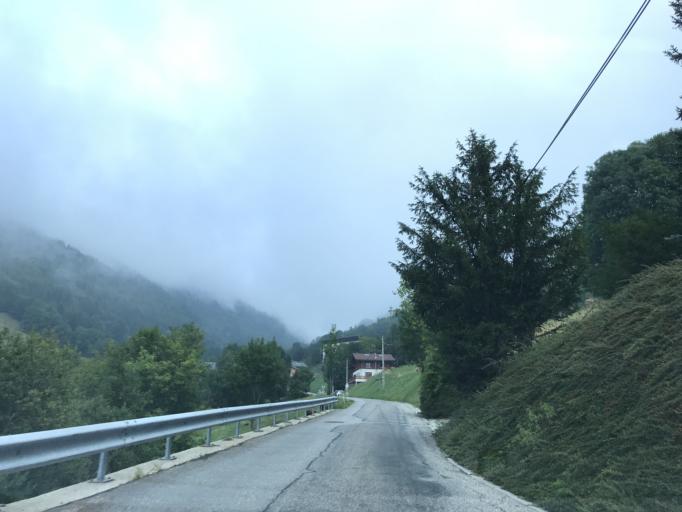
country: FR
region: Rhone-Alpes
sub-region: Departement de la Haute-Savoie
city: Doussard
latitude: 45.8088
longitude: 6.2619
